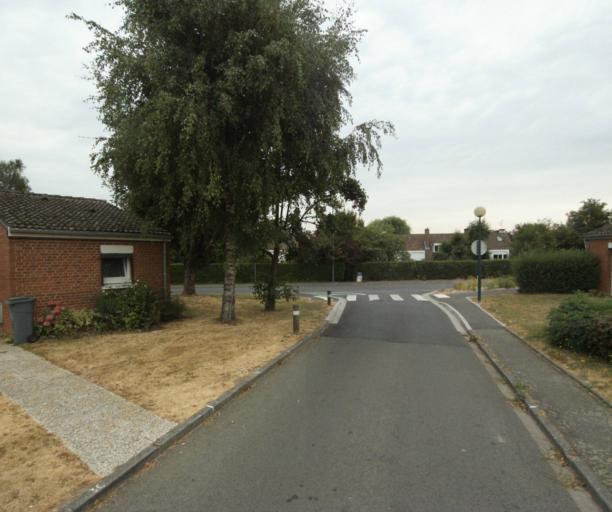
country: FR
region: Nord-Pas-de-Calais
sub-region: Departement du Nord
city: Bondues
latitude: 50.7032
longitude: 3.0890
